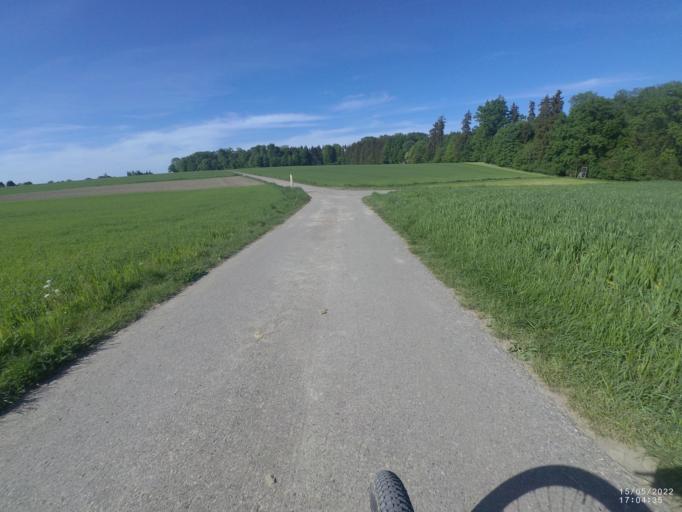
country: DE
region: Baden-Wuerttemberg
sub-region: Regierungsbezirk Stuttgart
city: Bolheim
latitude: 48.5852
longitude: 10.1424
